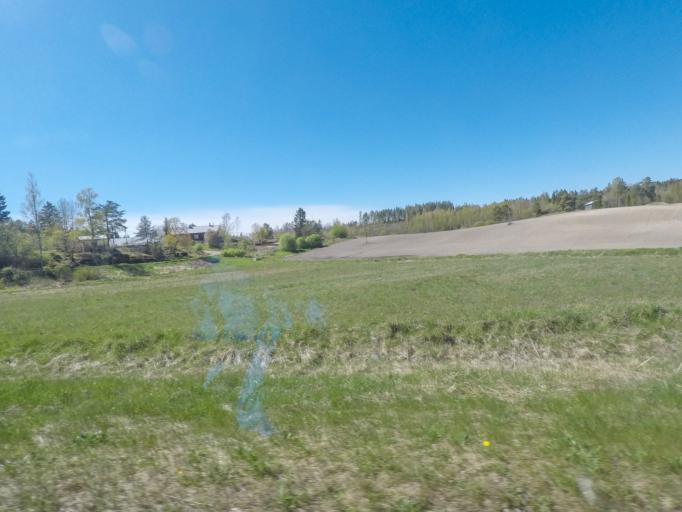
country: FI
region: Uusimaa
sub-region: Helsinki
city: Sammatti
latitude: 60.3605
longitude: 23.8027
